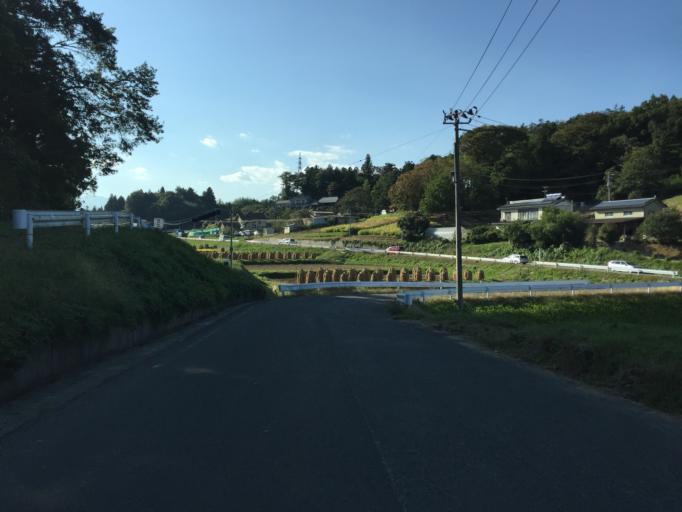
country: JP
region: Fukushima
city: Fukushima-shi
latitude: 37.6596
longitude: 140.5000
